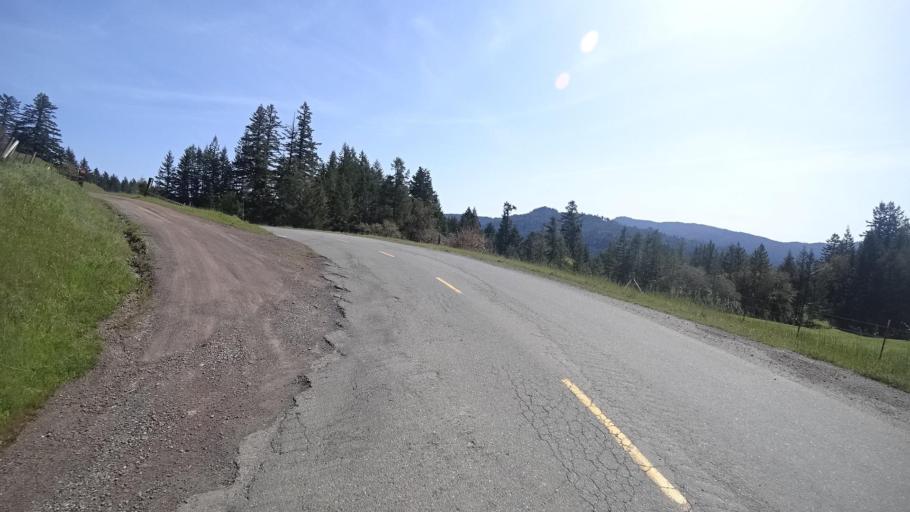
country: US
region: California
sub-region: Humboldt County
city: Redway
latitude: 40.4152
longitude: -123.7624
